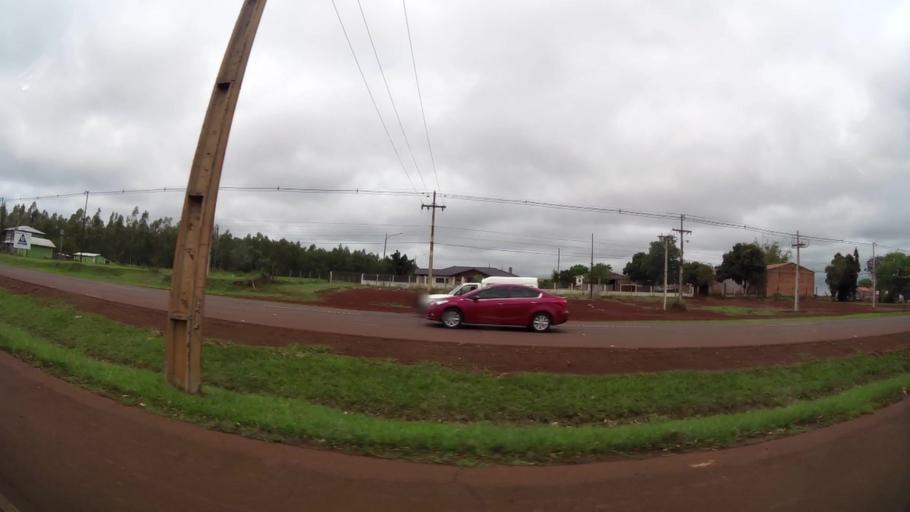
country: PY
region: Alto Parana
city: Presidente Franco
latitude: -25.4911
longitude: -54.7575
